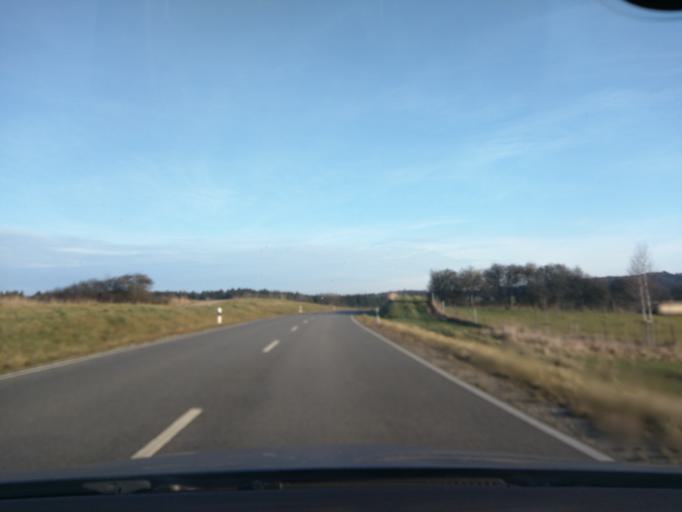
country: DE
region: Bavaria
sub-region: Upper Bavaria
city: Au in der Hallertau
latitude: 48.5622
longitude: 11.7297
